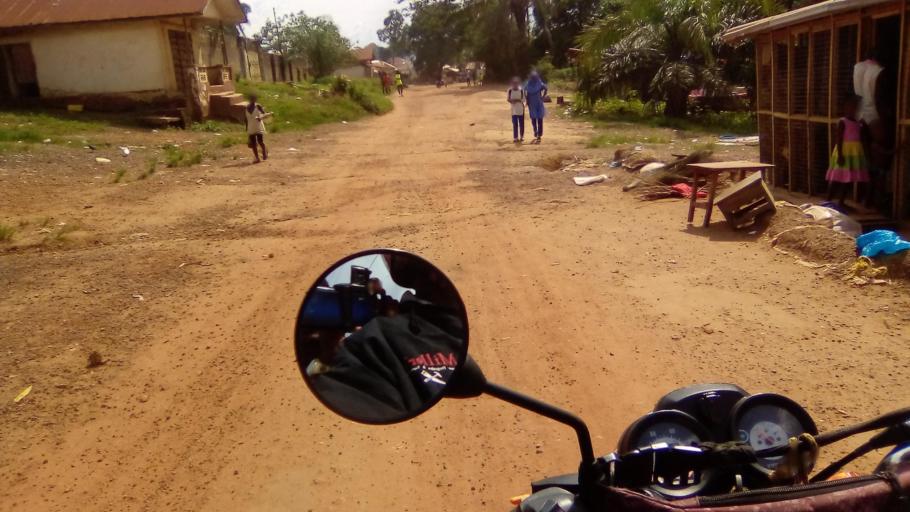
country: SL
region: Southern Province
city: Bo
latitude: 7.9525
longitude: -11.7291
